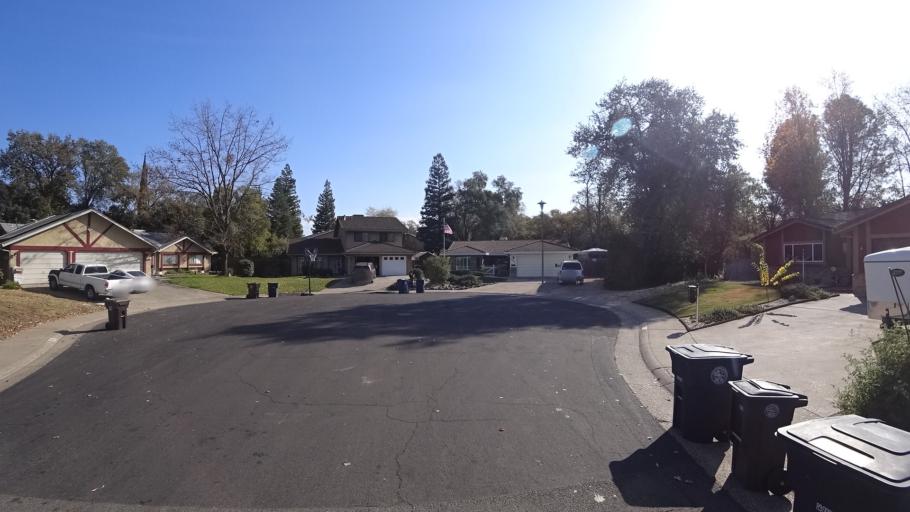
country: US
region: California
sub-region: Sacramento County
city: Citrus Heights
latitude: 38.6874
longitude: -121.2680
